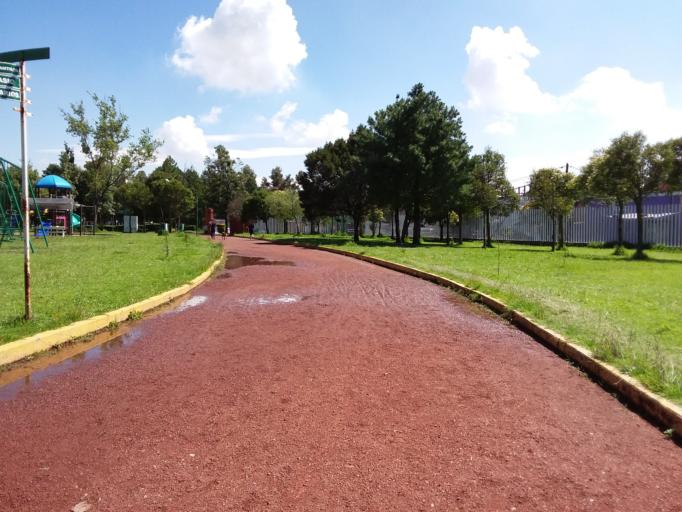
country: MX
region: Mexico
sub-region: Metepec
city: San Salvador Tizatlalli
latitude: 19.2595
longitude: -99.5863
